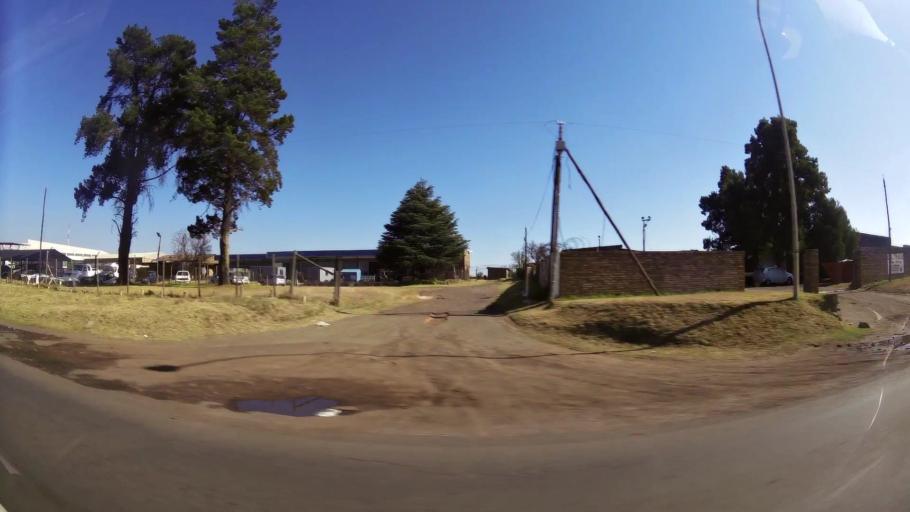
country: ZA
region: Mpumalanga
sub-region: Nkangala District Municipality
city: Witbank
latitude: -25.8546
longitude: 29.2326
